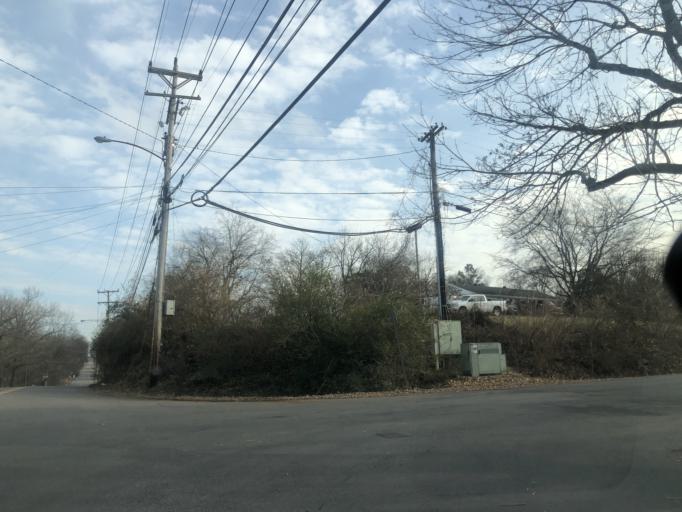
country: US
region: Tennessee
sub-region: Davidson County
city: Oak Hill
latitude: 36.1055
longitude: -86.7065
